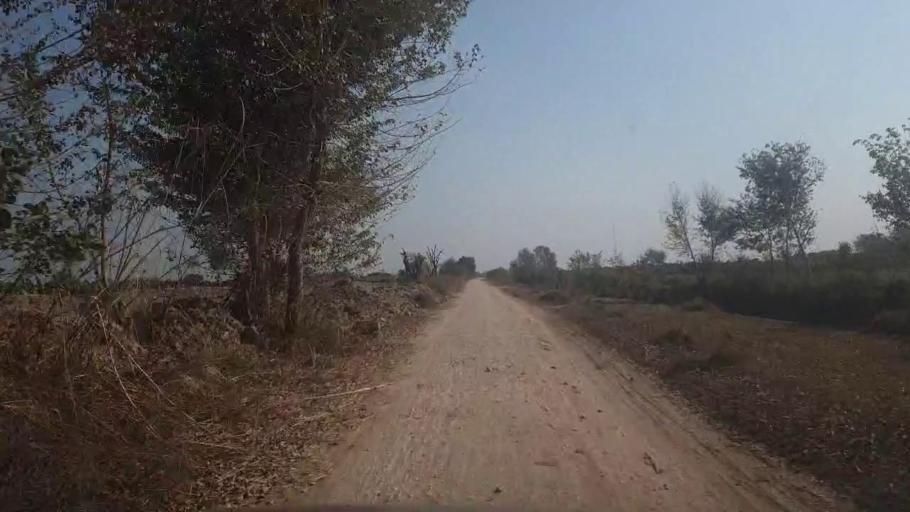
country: PK
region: Sindh
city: Sakrand
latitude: 26.0700
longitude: 68.4294
